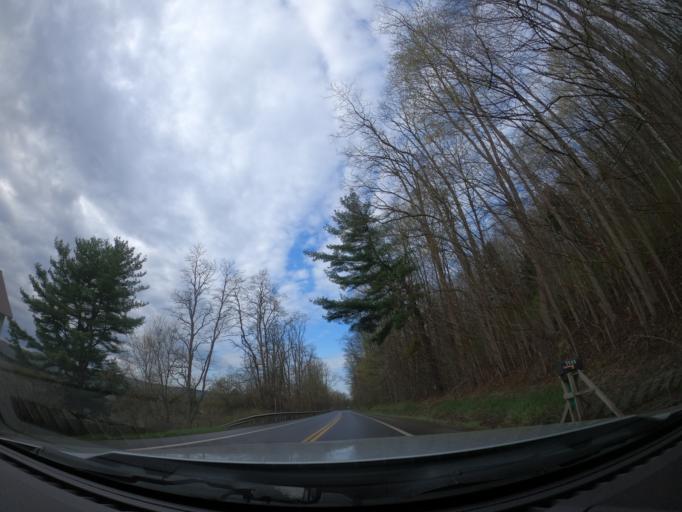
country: US
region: New York
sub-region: Cortland County
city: McGraw
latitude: 42.6609
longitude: -76.1117
